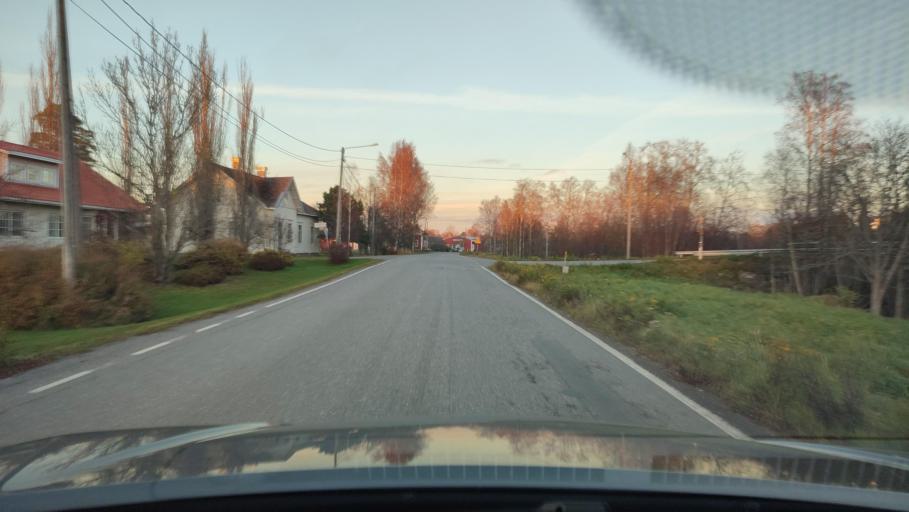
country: FI
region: Ostrobothnia
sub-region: Sydosterbotten
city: Kristinestad
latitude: 62.3026
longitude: 21.4527
